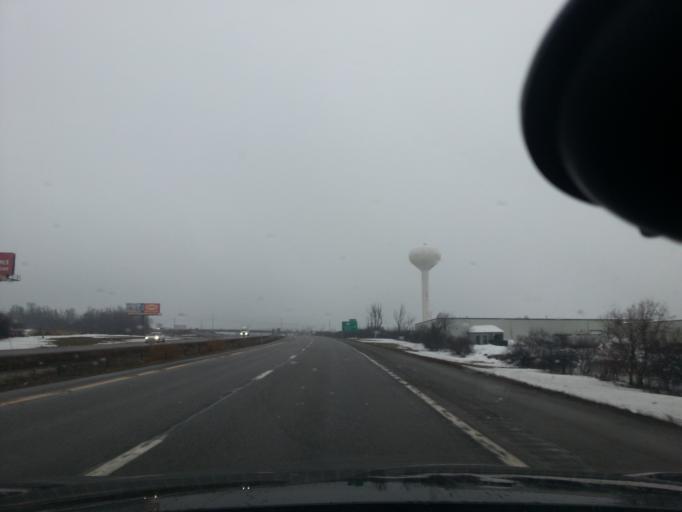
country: US
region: New York
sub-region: Jefferson County
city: Watertown
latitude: 43.9929
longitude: -75.9394
